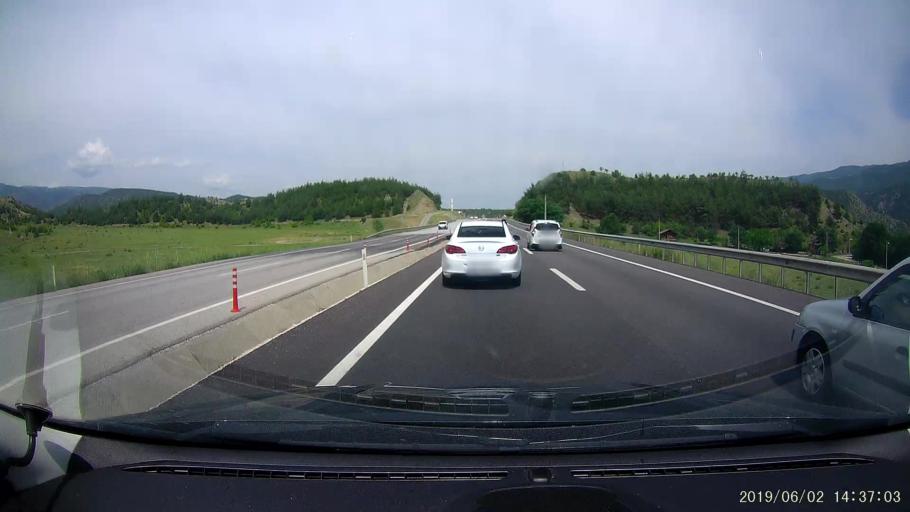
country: TR
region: Corum
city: Hacihamza
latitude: 41.0498
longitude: 34.2491
